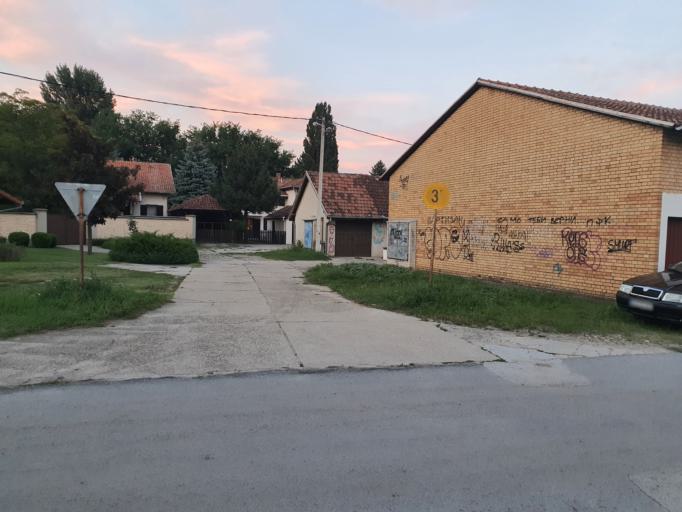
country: RS
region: Autonomna Pokrajina Vojvodina
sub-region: Severnobacki Okrug
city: Subotica
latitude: 46.1079
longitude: 19.6752
